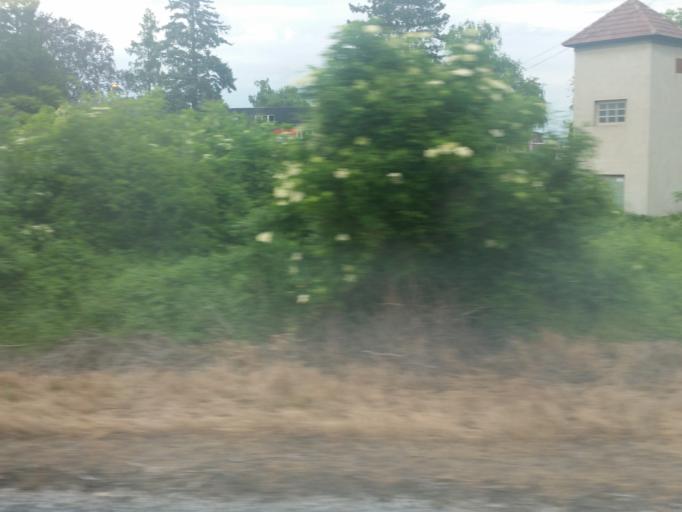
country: AT
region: Lower Austria
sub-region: Politischer Bezirk Ganserndorf
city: Raasdorf
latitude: 48.2392
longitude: 16.5807
